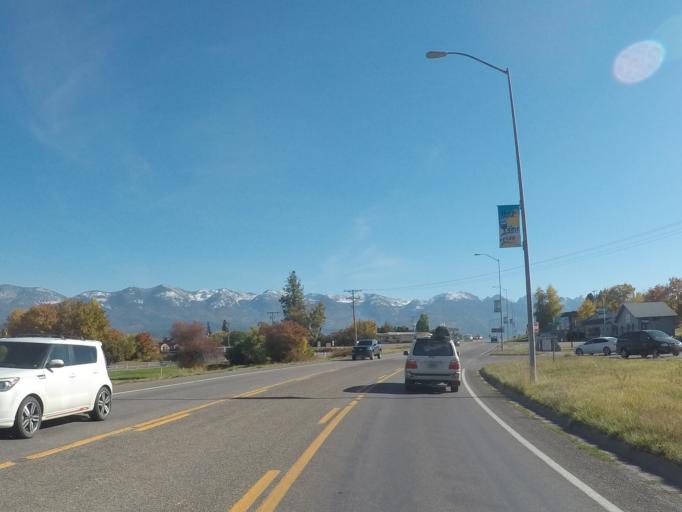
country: US
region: Montana
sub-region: Lake County
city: Polson
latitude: 47.6933
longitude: -114.1312
